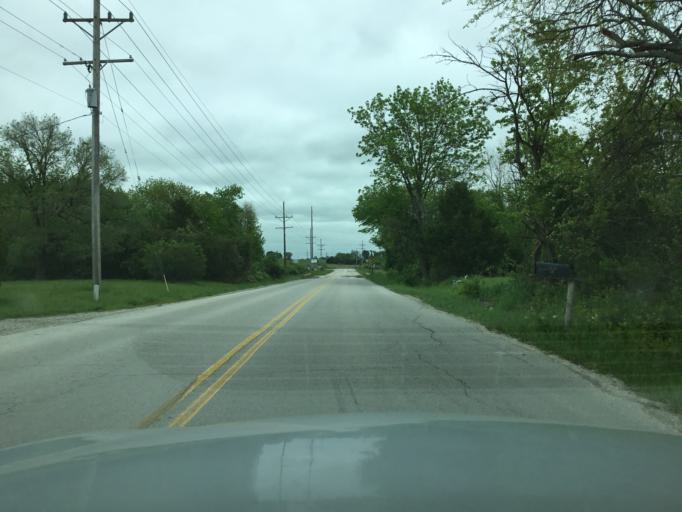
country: US
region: Kansas
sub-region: Franklin County
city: Ottawa
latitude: 38.5793
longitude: -95.2623
